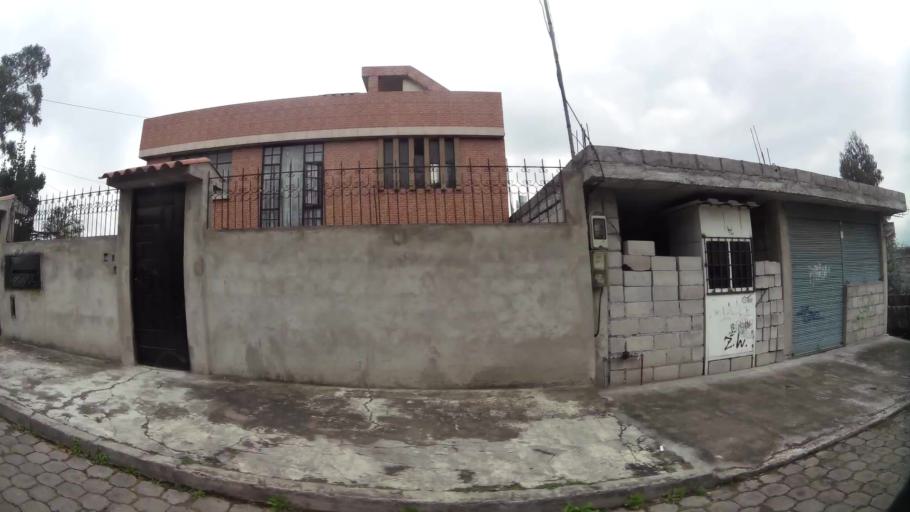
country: EC
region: Pichincha
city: Sangolqui
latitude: -0.2977
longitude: -78.4718
